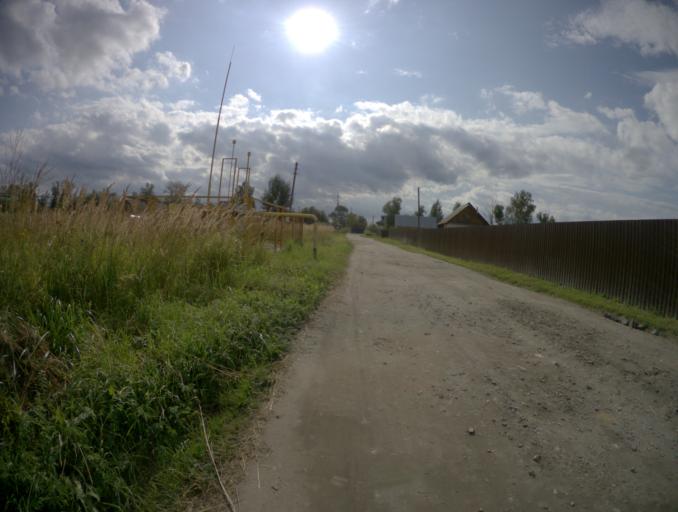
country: RU
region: Vladimir
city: Golovino
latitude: 55.9537
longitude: 40.4342
